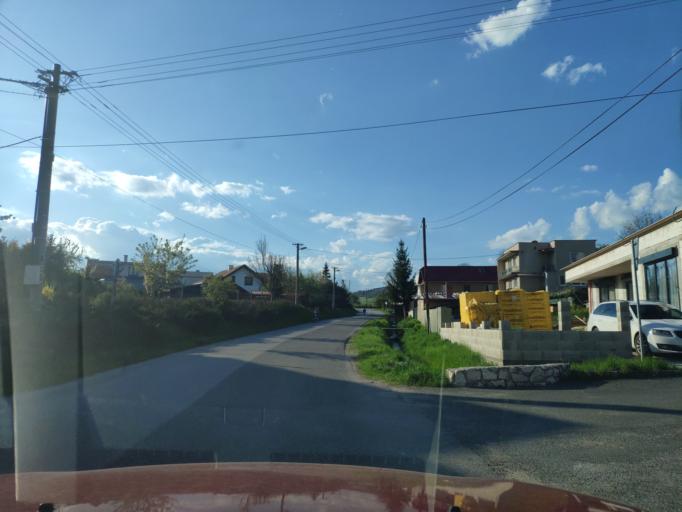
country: SK
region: Presovsky
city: Spisske Podhradie
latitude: 49.0254
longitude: 20.7981
